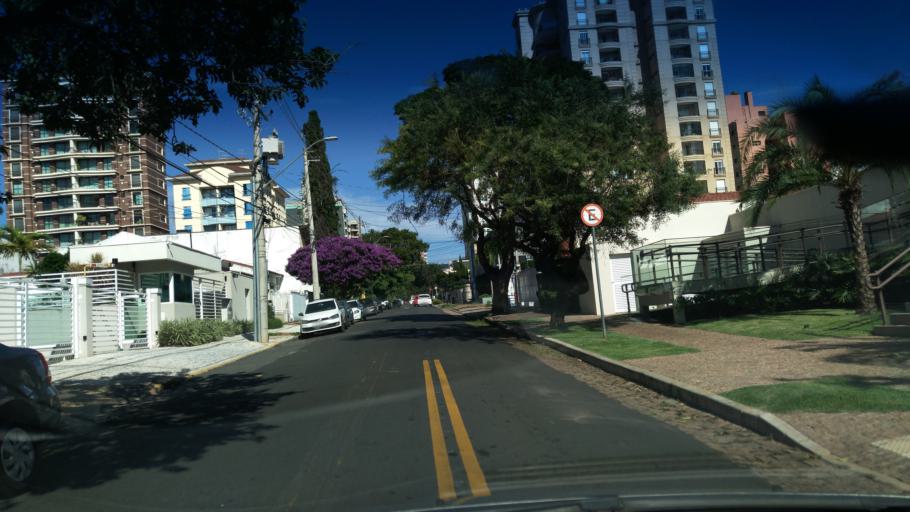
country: BR
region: Sao Paulo
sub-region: Campinas
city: Campinas
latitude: -22.8911
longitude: -47.0491
